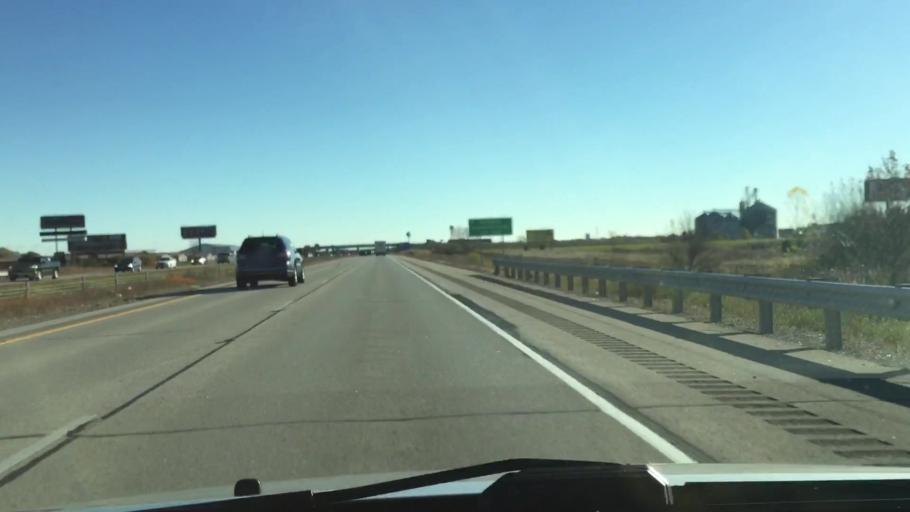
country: US
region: Wisconsin
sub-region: Outagamie County
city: Little Chute
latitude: 44.2978
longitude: -88.3310
